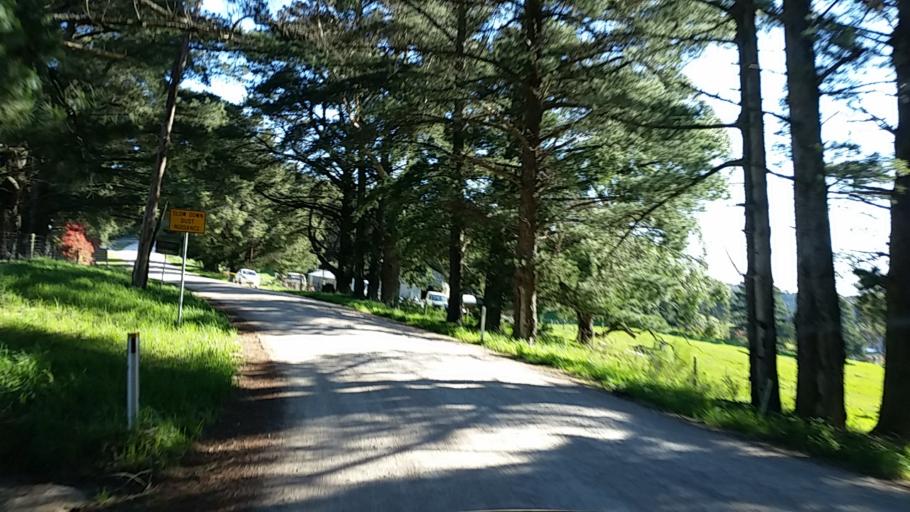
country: AU
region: South Australia
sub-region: Adelaide Hills
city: Lobethal
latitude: -34.8964
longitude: 138.8225
